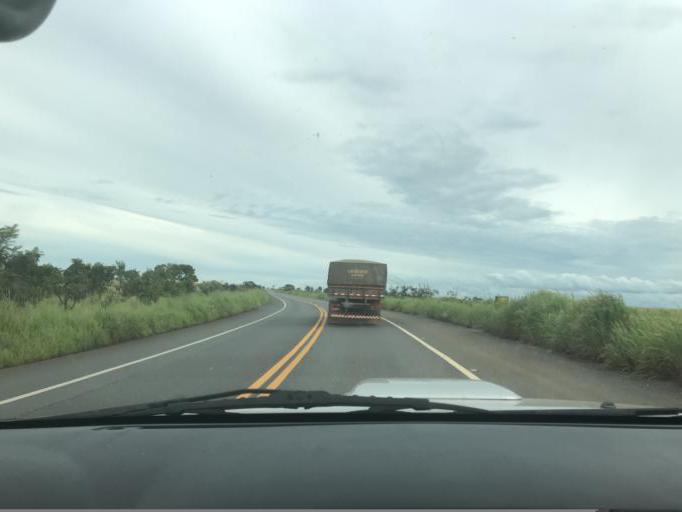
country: BR
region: Minas Gerais
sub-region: Araxa
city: Araxa
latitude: -19.3850
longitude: -46.8602
